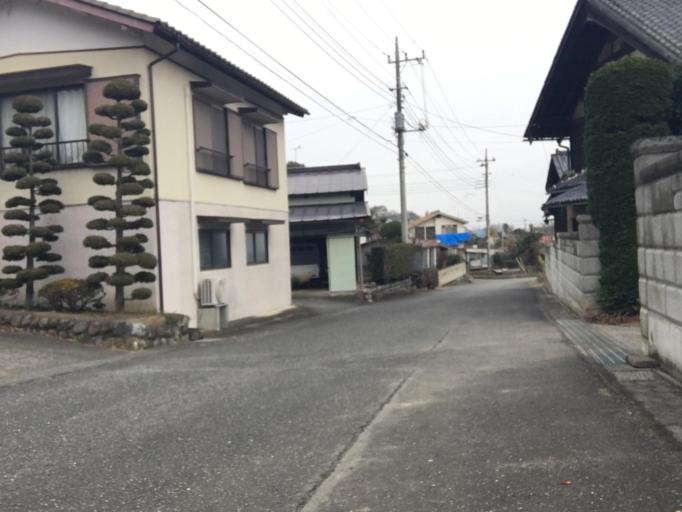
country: JP
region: Saitama
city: Yorii
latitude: 36.1332
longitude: 139.1991
